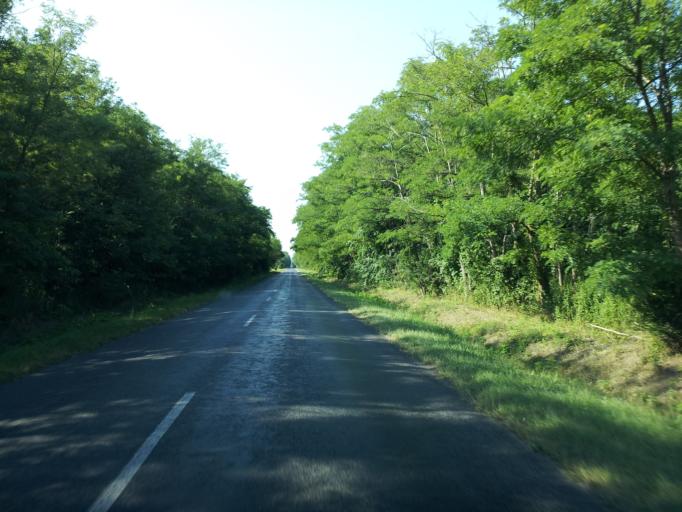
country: HU
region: Zala
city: Cserszegtomaj
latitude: 46.8565
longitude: 17.1989
